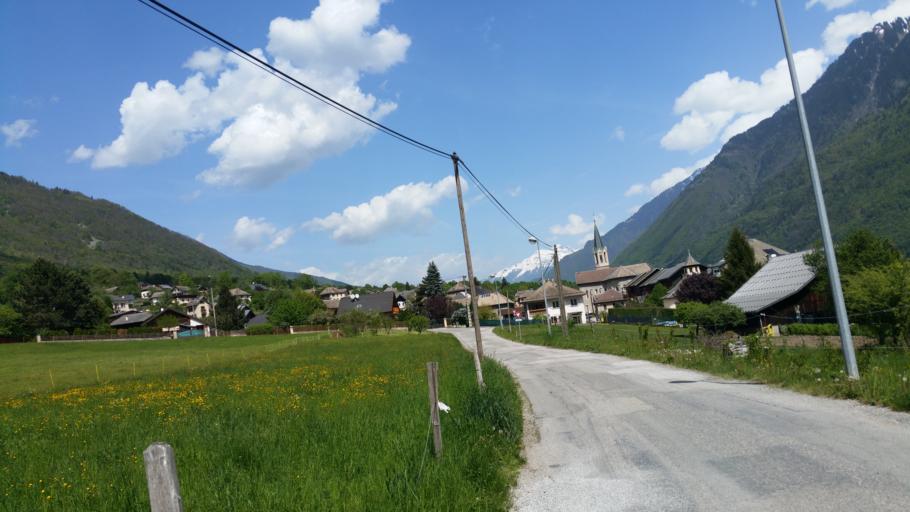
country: FR
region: Rhone-Alpes
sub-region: Departement de la Savoie
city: Saint-Remy-de-Maurienne
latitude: 45.3905
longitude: 6.2646
